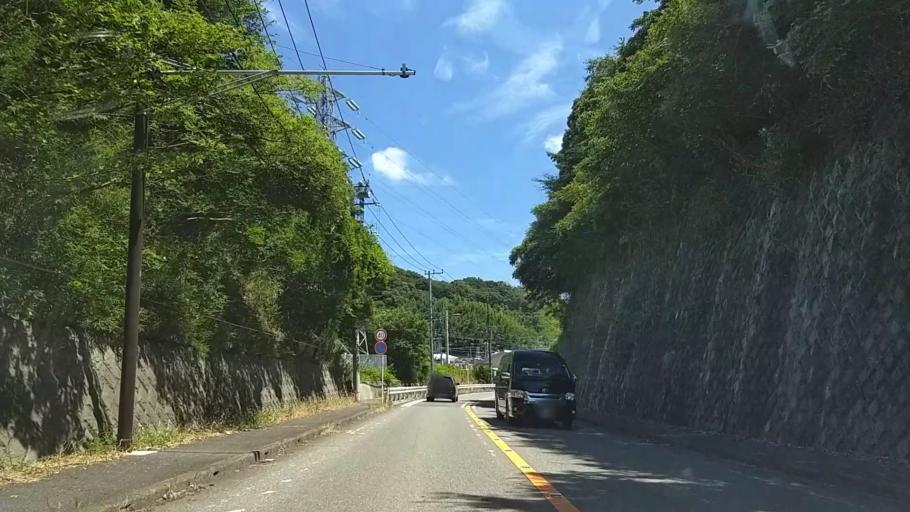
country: JP
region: Kanagawa
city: Zushi
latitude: 35.3057
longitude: 139.5681
